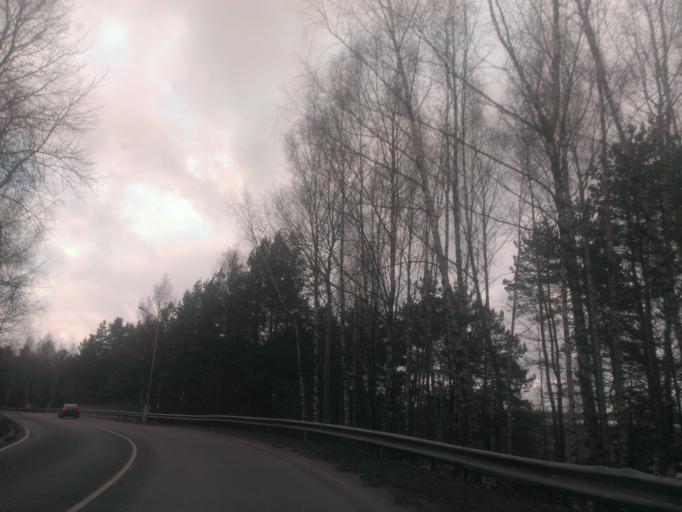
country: LV
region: Riga
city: Bergi
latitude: 56.9998
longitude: 24.2794
